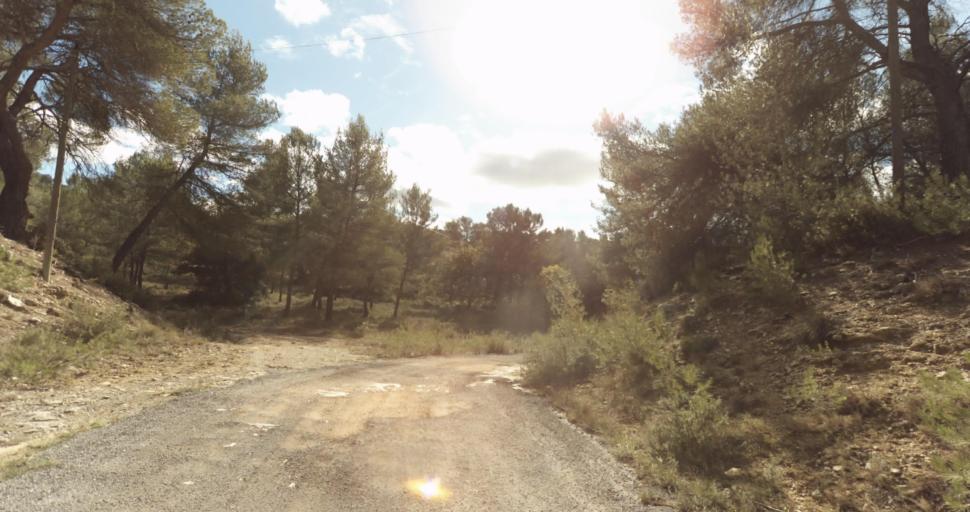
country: FR
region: Provence-Alpes-Cote d'Azur
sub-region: Departement des Bouches-du-Rhone
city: Venelles
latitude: 43.6024
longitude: 5.4976
